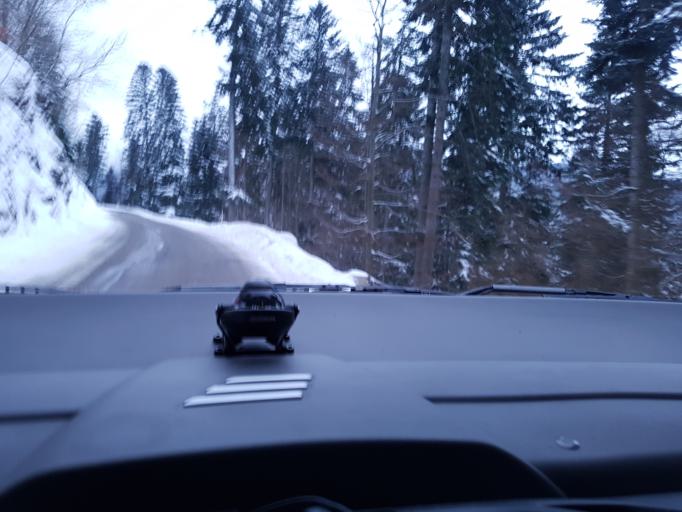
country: FR
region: Alsace
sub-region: Departement du Haut-Rhin
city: Lapoutroie
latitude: 48.1977
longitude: 7.1312
